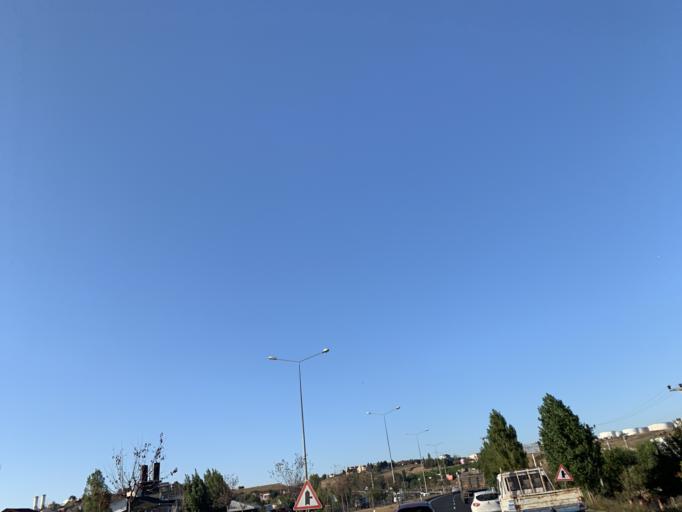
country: TR
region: Tekirdag
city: Sultankoy
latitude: 41.0084
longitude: 27.9802
